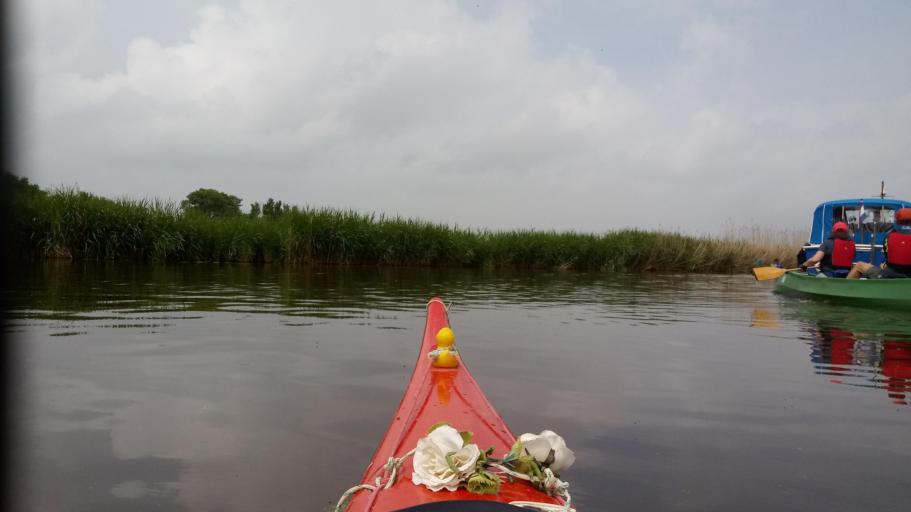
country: NL
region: Groningen
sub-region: Gemeente Bedum
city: Bedum
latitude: 53.3367
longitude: 6.5853
